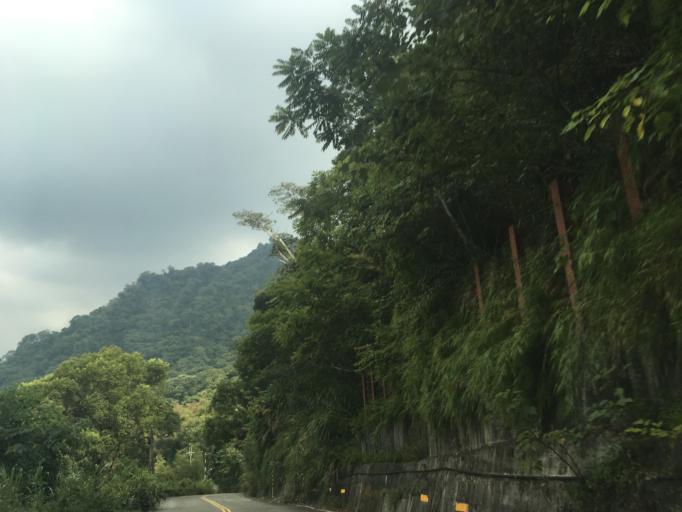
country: TW
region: Taiwan
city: Fengyuan
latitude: 24.3363
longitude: 120.9293
